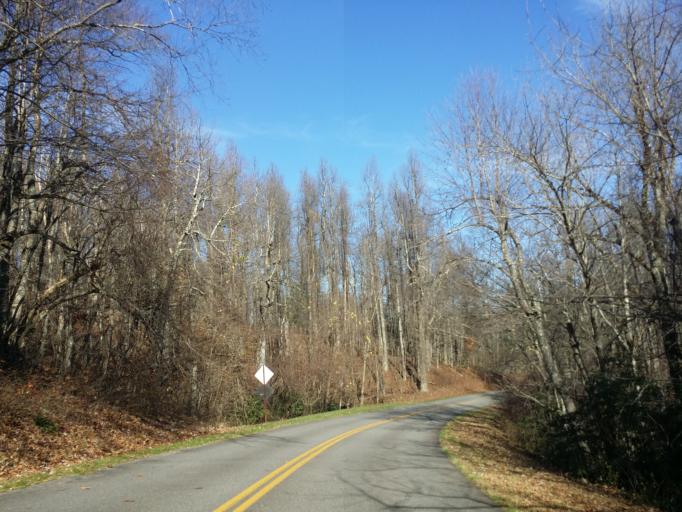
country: US
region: North Carolina
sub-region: Mitchell County
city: Spruce Pine
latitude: 35.8090
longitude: -82.1478
